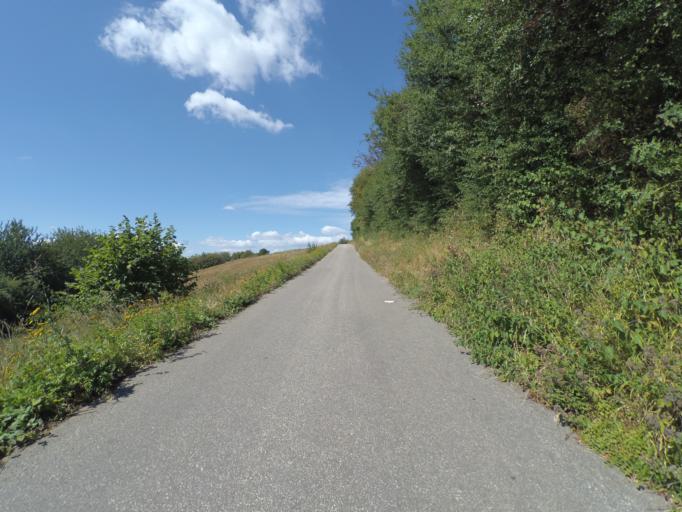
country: DE
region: Rheinland-Pfalz
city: Merzkirchen
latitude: 49.5949
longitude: 6.4986
